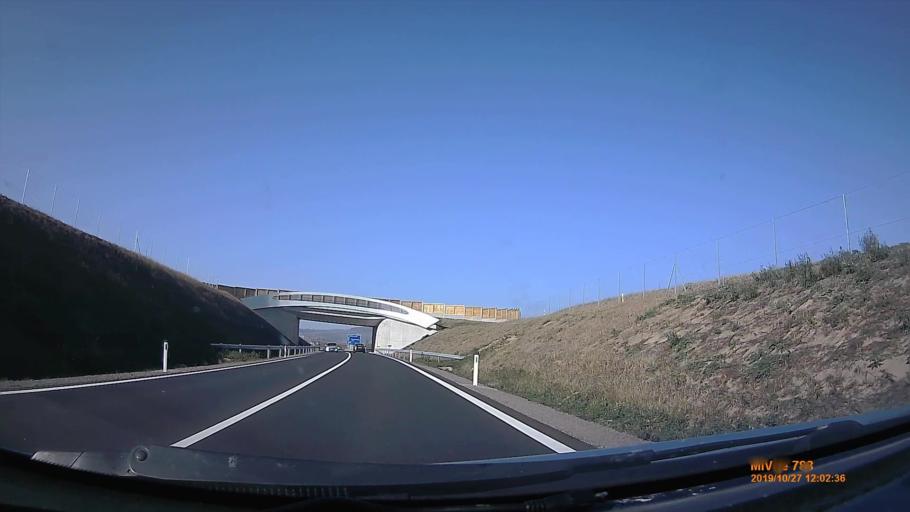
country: AT
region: Lower Austria
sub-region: Politischer Bezirk Mistelbach
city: Drasenhofen
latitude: 48.7361
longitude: 16.6492
